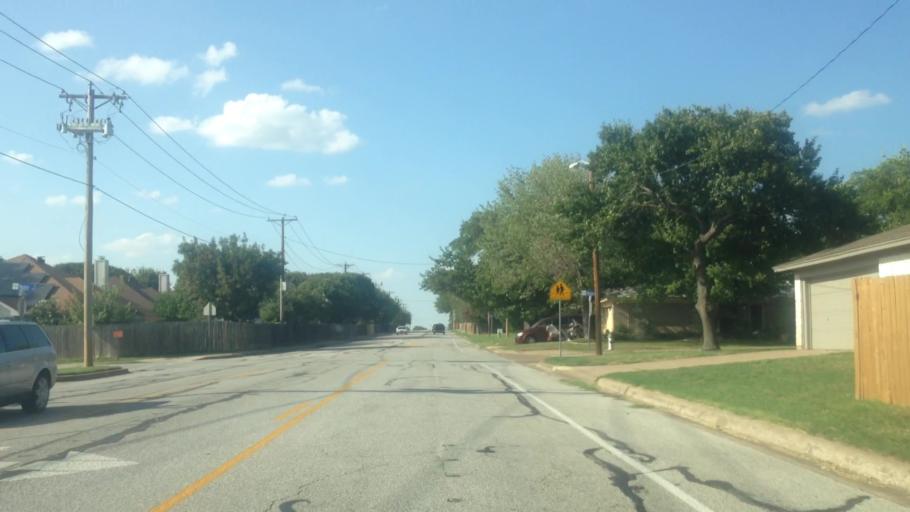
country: US
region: Texas
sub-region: Tarrant County
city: Watauga
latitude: 32.8759
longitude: -97.2550
